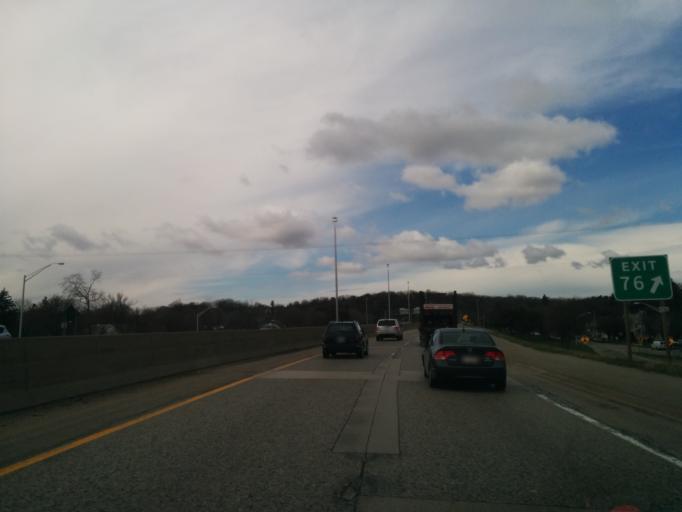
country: US
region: Michigan
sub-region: Kent County
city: Grand Rapids
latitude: 42.9727
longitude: -85.6887
